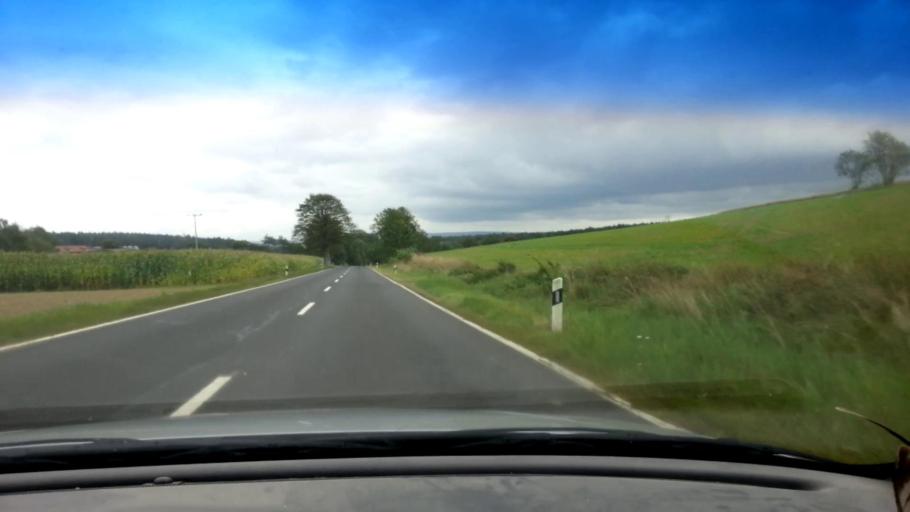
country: DE
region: Bavaria
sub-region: Upper Palatinate
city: Waldsassen
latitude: 50.0353
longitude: 12.2953
